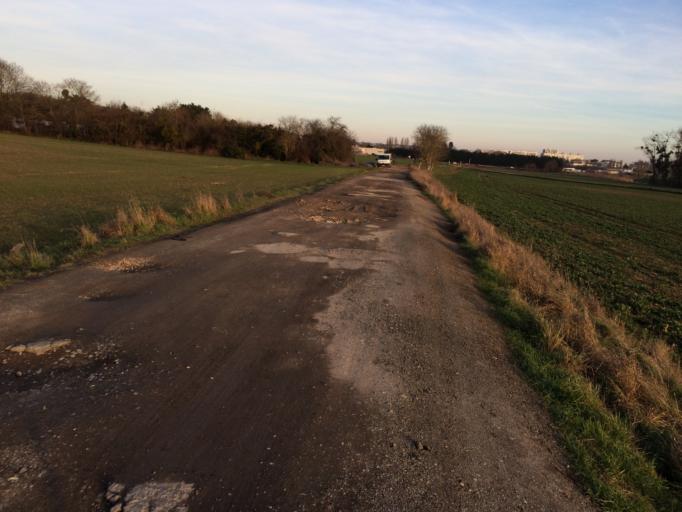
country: FR
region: Ile-de-France
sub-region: Departement de l'Essonne
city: Champlan
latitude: 48.7021
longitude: 2.2780
